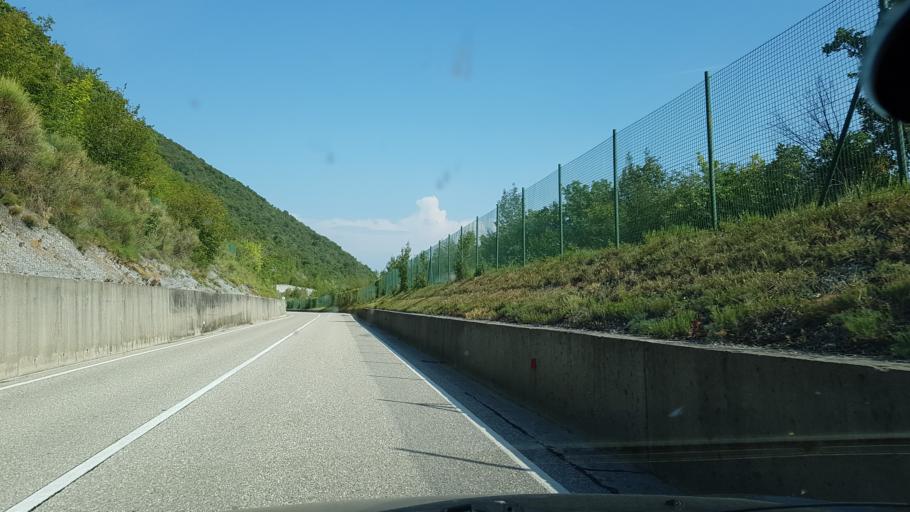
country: SI
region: Nova Gorica
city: Solkan
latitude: 45.9827
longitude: 13.6289
